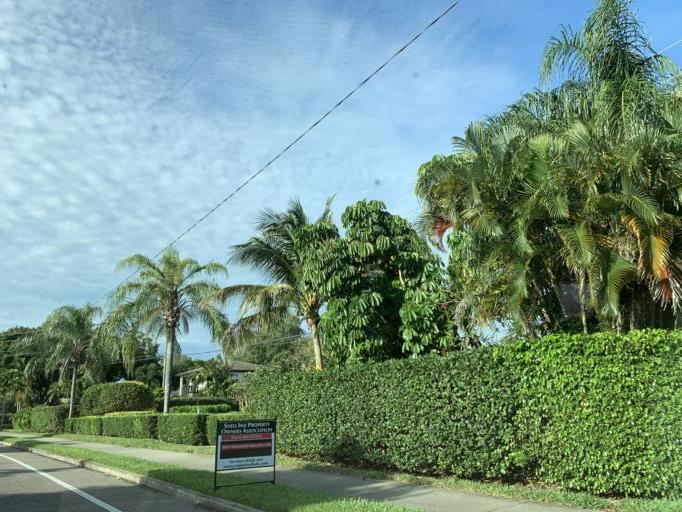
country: US
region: Florida
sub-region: Pinellas County
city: Gandy
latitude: 27.7992
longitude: -82.6106
